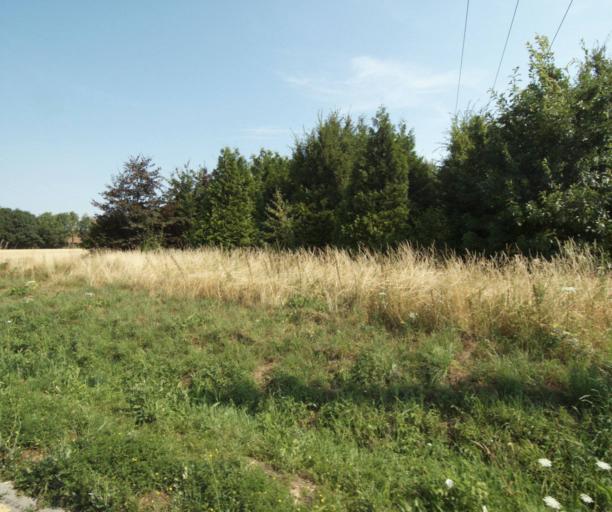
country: FR
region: Nord-Pas-de-Calais
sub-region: Departement du Nord
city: Comines
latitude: 50.7541
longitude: 3.0168
